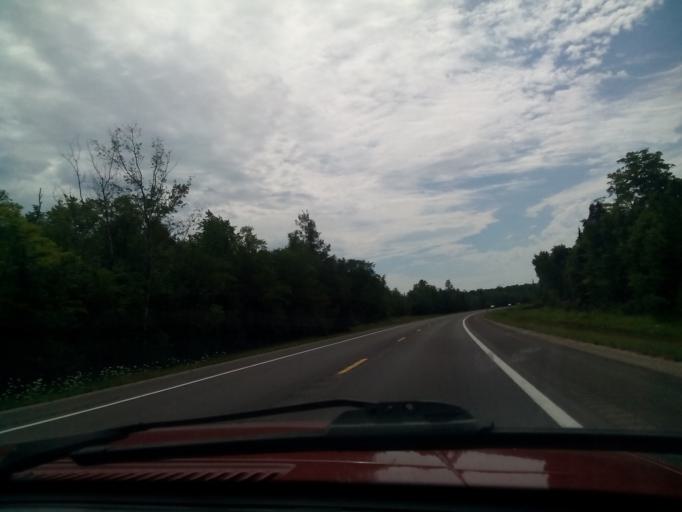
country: US
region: Michigan
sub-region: Schoolcraft County
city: Manistique
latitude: 46.0631
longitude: -85.9585
